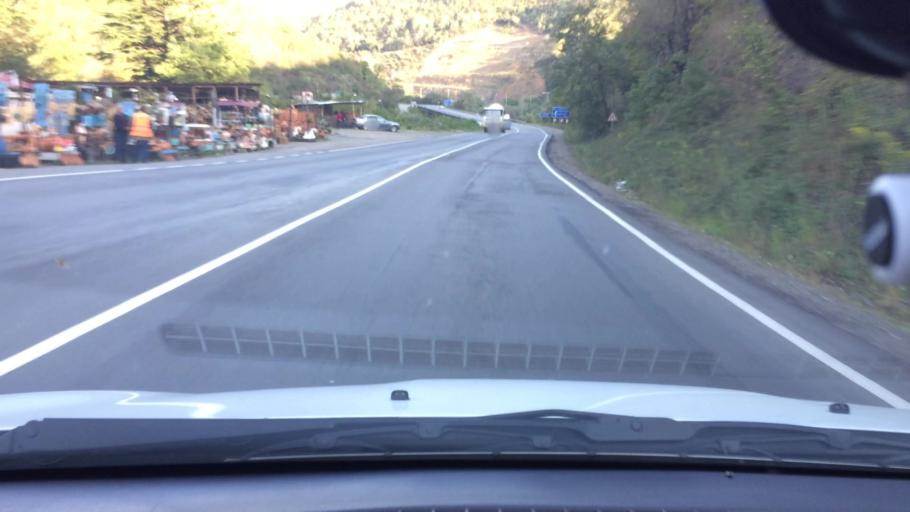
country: GE
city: Shorapani
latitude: 42.0827
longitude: 43.1423
